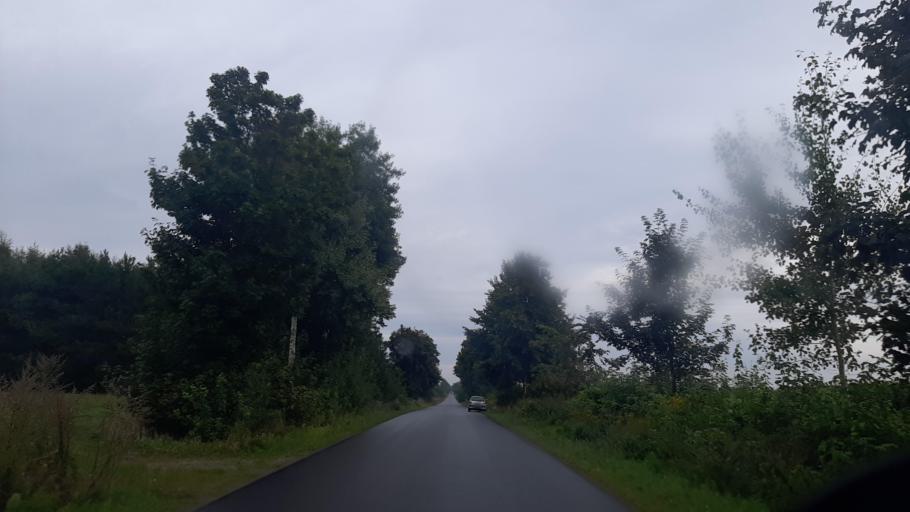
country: PL
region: Lublin Voivodeship
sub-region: Powiat lubartowski
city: Kamionka
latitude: 51.4670
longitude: 22.4433
